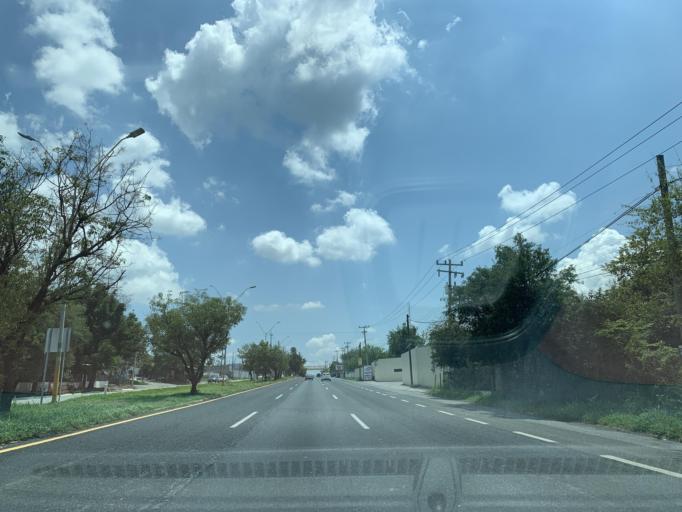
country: MX
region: Nuevo Leon
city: Santiago
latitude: 25.3938
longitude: -100.1213
